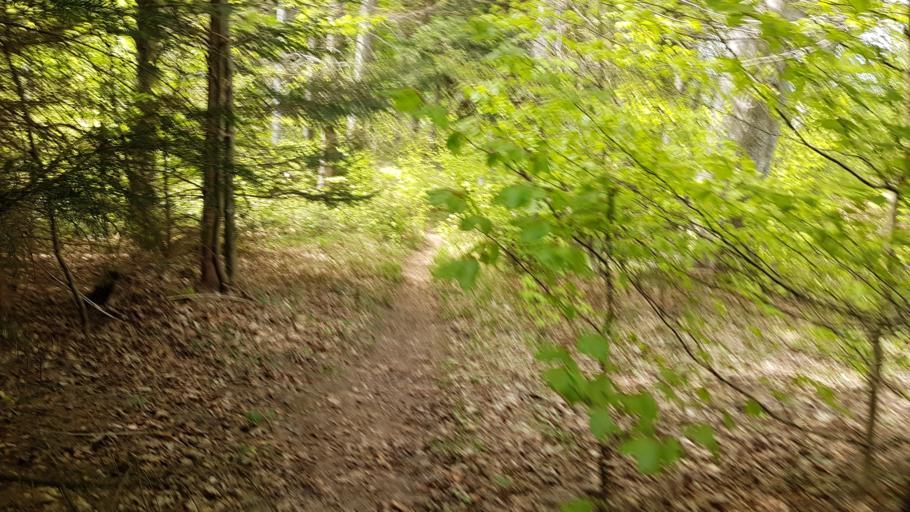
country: CH
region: Aargau
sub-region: Bezirk Kulm
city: Reinach
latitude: 47.2850
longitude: 8.1802
